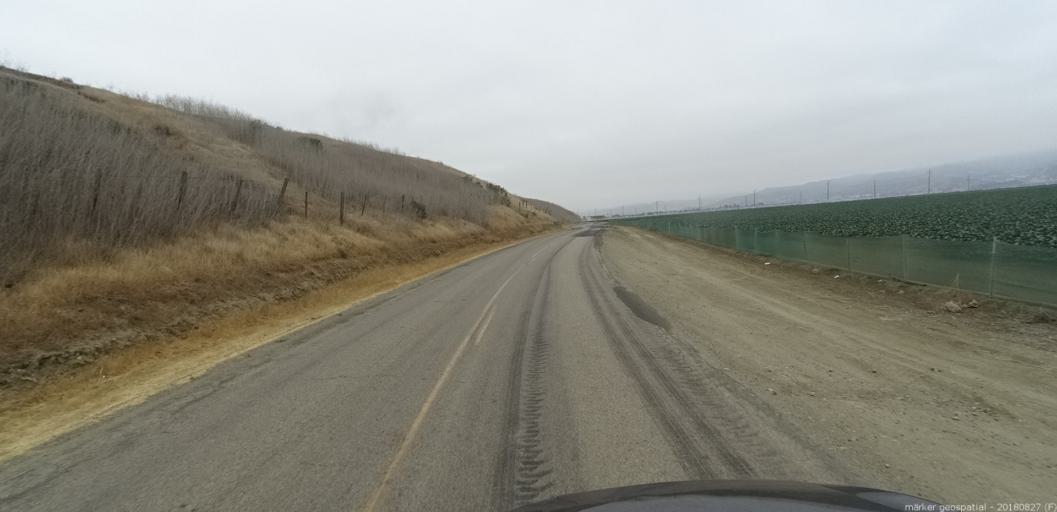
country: US
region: California
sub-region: Monterey County
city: King City
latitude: 36.2357
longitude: -121.1286
